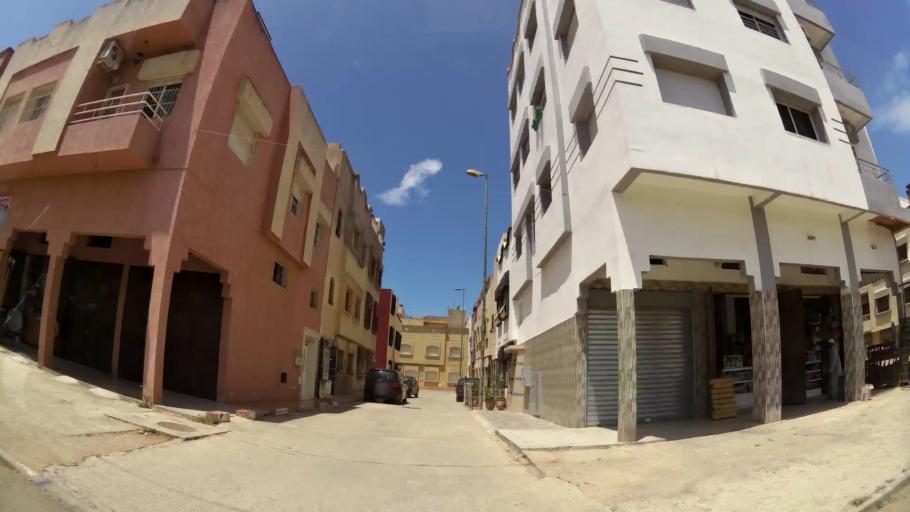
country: MA
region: Gharb-Chrarda-Beni Hssen
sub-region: Kenitra Province
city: Kenitra
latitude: 34.2514
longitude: -6.6122
